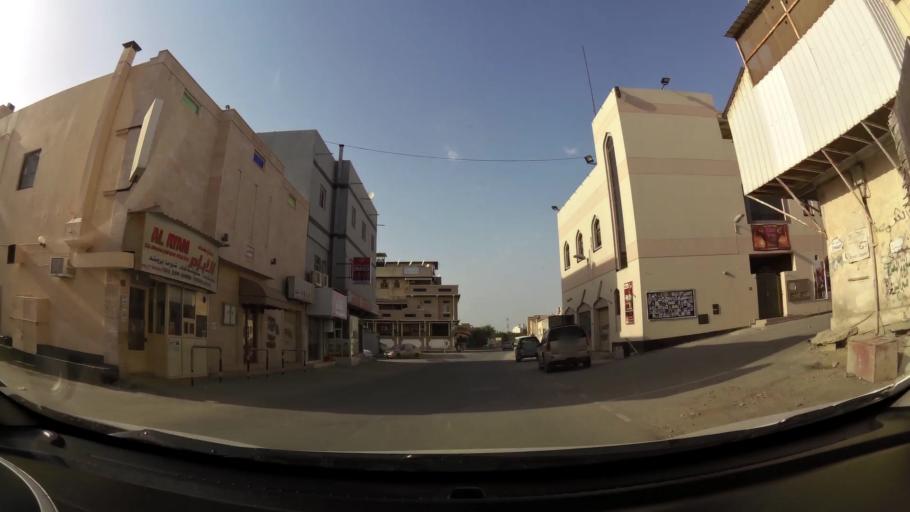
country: BH
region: Manama
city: Jidd Hafs
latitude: 26.2125
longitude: 50.5040
